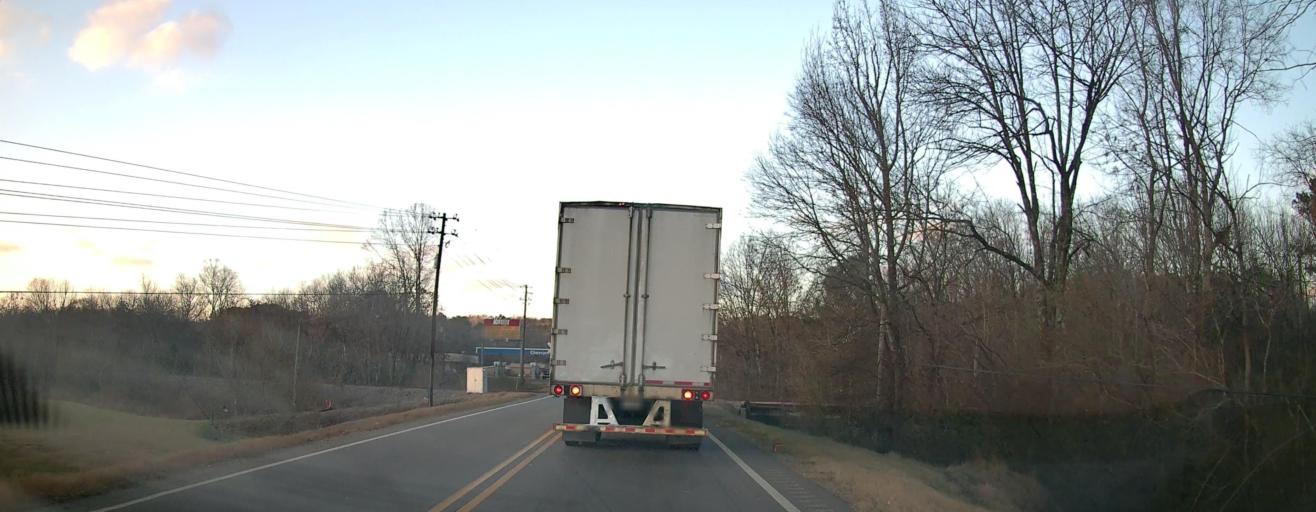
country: US
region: Alabama
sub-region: Etowah County
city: Attalla
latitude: 34.0335
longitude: -86.1190
